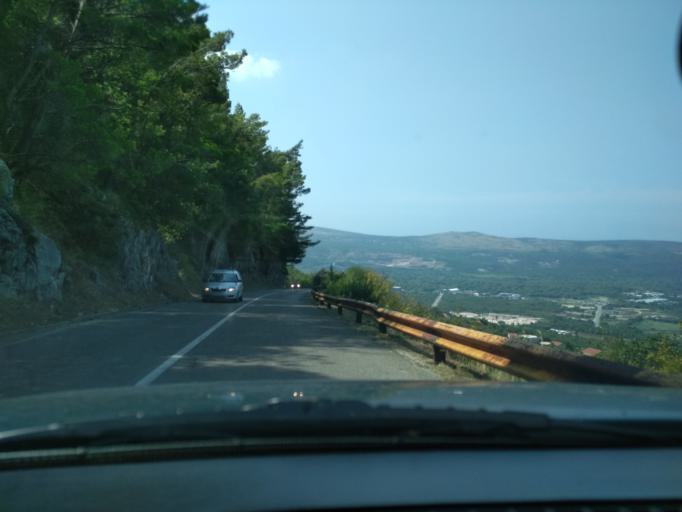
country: ME
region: Kotor
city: Kotor
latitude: 42.4016
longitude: 18.7599
